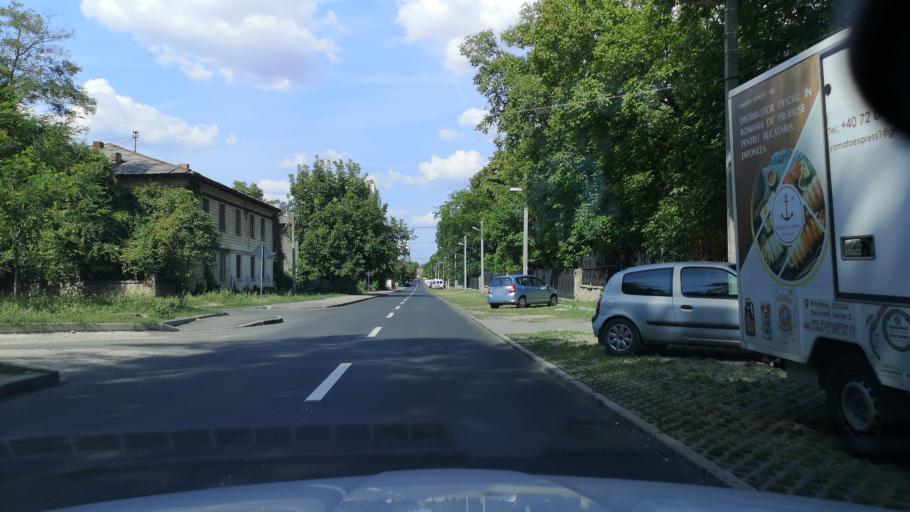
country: MD
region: Chisinau
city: Chisinau
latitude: 47.0249
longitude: 28.8089
